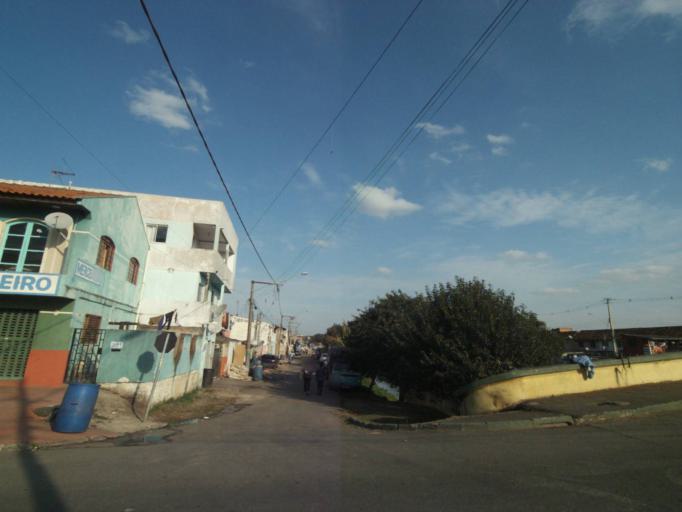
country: BR
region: Parana
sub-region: Curitiba
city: Curitiba
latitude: -25.4434
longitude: -49.2518
